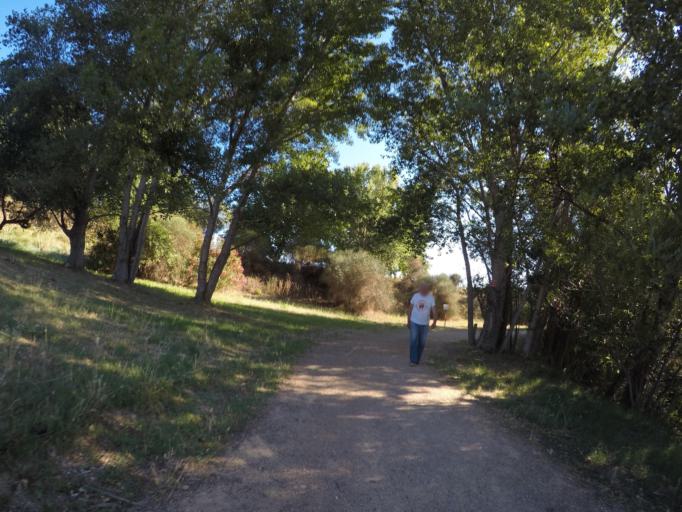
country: FR
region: Languedoc-Roussillon
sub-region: Departement des Pyrenees-Orientales
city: Pezilla-la-Riviere
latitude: 42.6821
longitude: 2.7548
